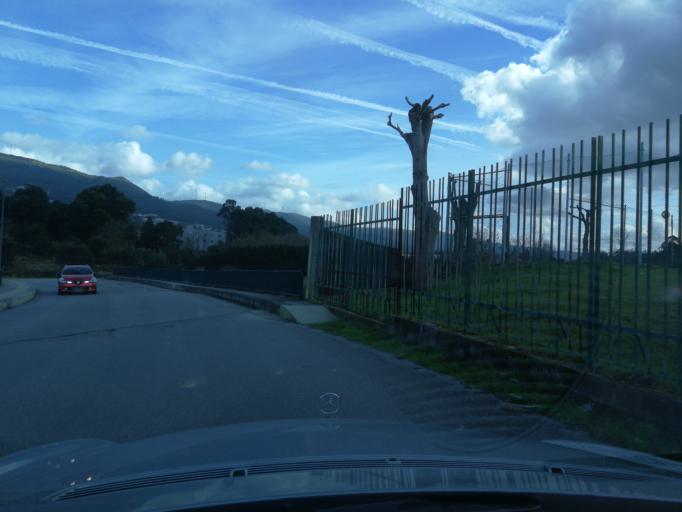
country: PT
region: Viana do Castelo
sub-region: Valenca
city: Valenza
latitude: 42.0302
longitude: -8.6379
